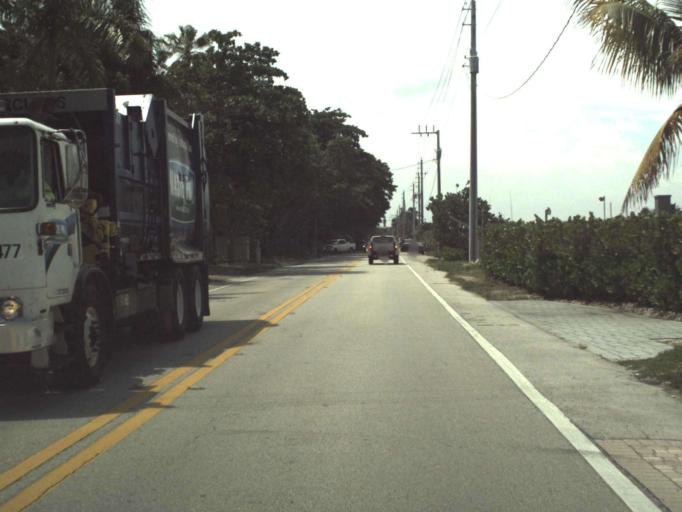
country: US
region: Florida
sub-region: Broward County
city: Lighthouse Point
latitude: 26.2737
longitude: -80.0804
